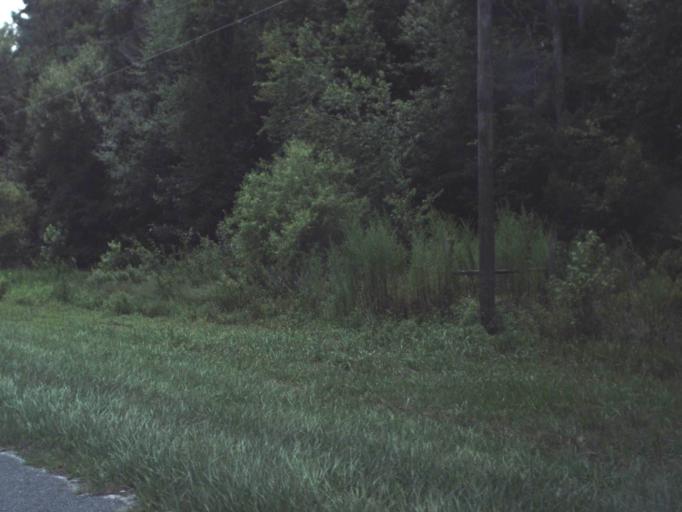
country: US
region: Florida
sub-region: Hamilton County
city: Jasper
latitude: 30.5982
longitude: -83.0122
